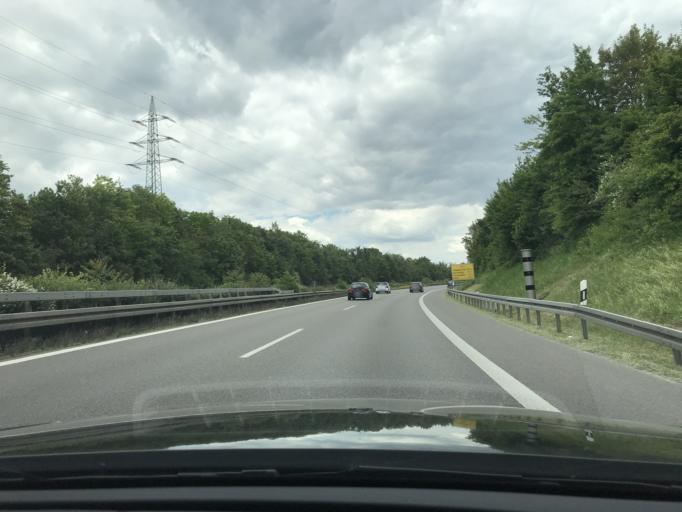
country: DE
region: Baden-Wuerttemberg
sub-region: Regierungsbezirk Stuttgart
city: Waiblingen
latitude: 48.8321
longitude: 9.3343
